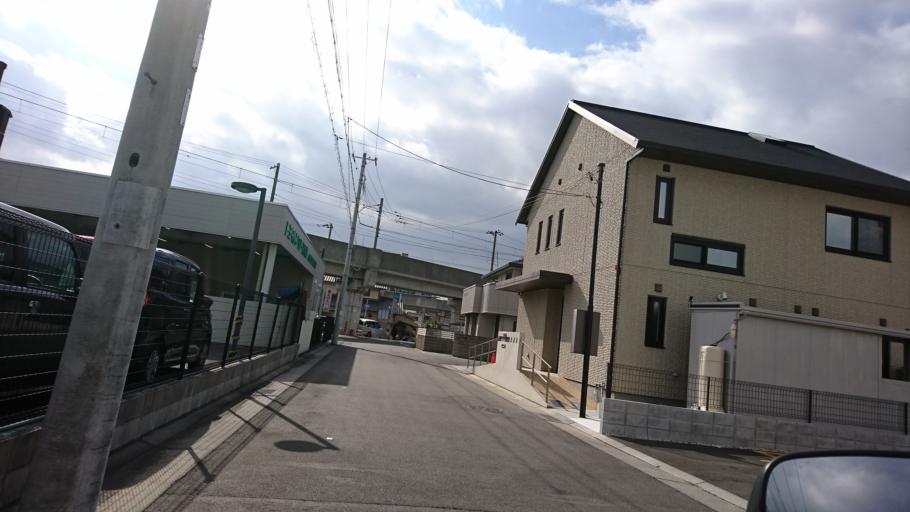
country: JP
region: Hyogo
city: Kakogawacho-honmachi
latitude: 34.7666
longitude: 134.8425
